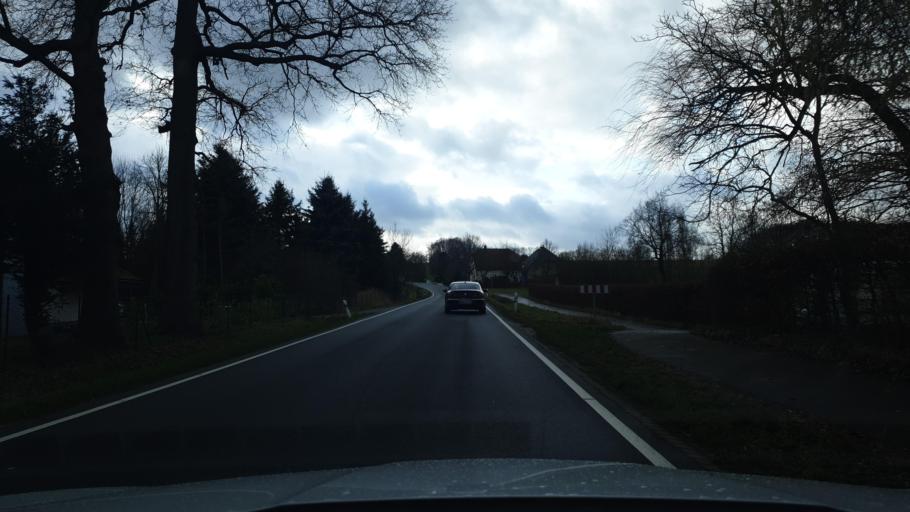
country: DE
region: North Rhine-Westphalia
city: Bad Oeynhausen
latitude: 52.1685
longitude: 8.8029
